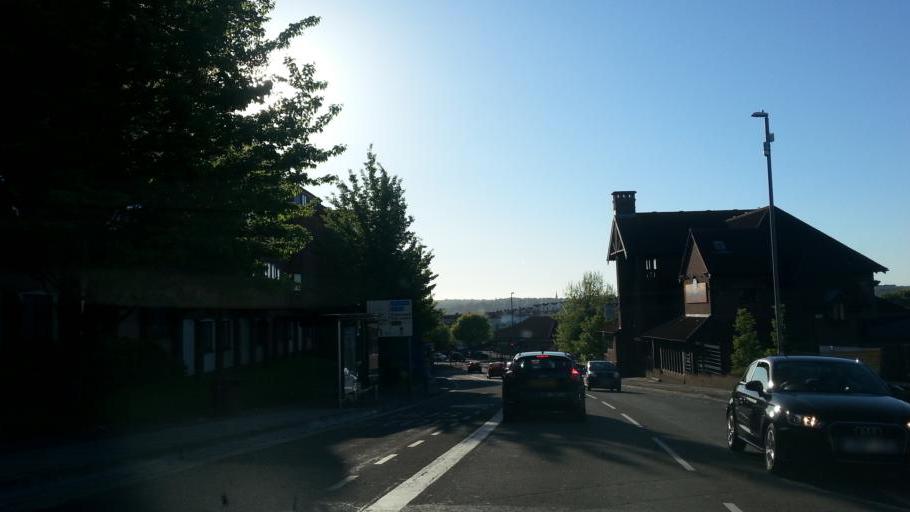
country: GB
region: England
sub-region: Bristol
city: Bristol
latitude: 51.4413
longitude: -2.5764
